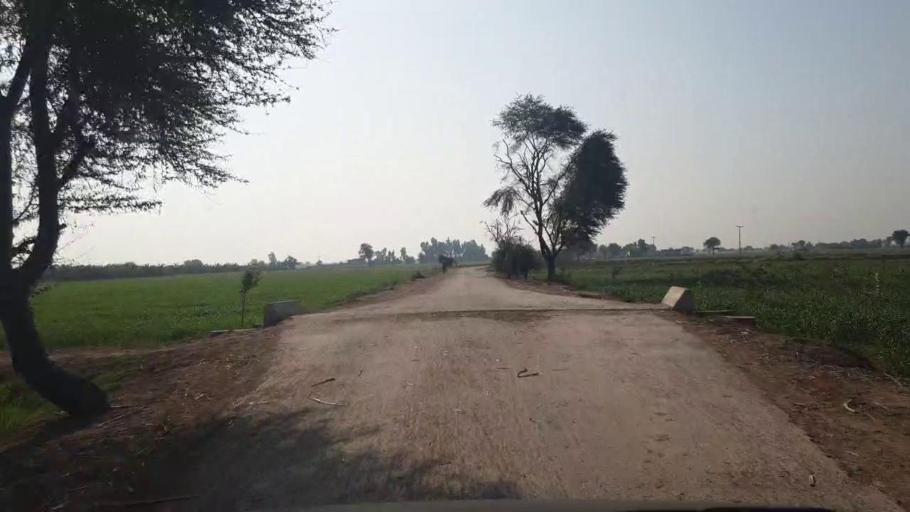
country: PK
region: Sindh
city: Bhit Shah
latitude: 25.7515
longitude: 68.5619
